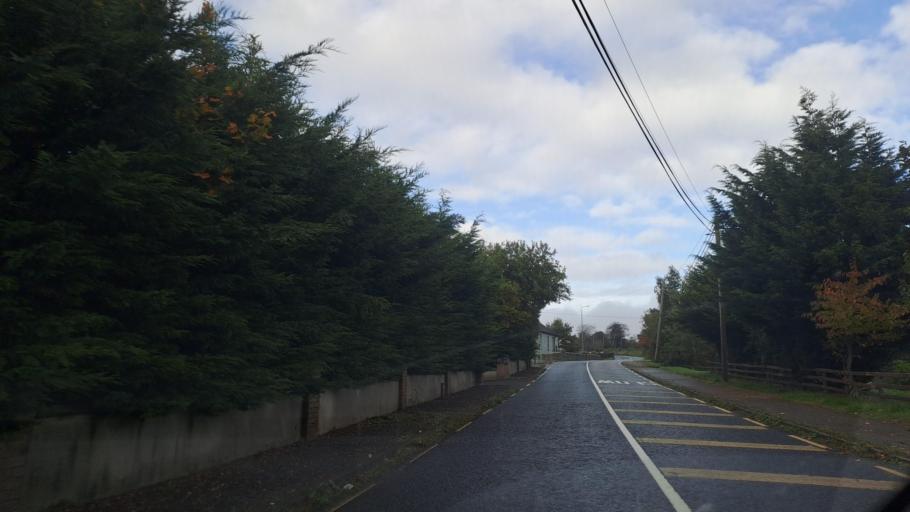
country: IE
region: Ulster
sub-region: County Monaghan
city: Carrickmacross
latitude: 53.9338
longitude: -6.7169
